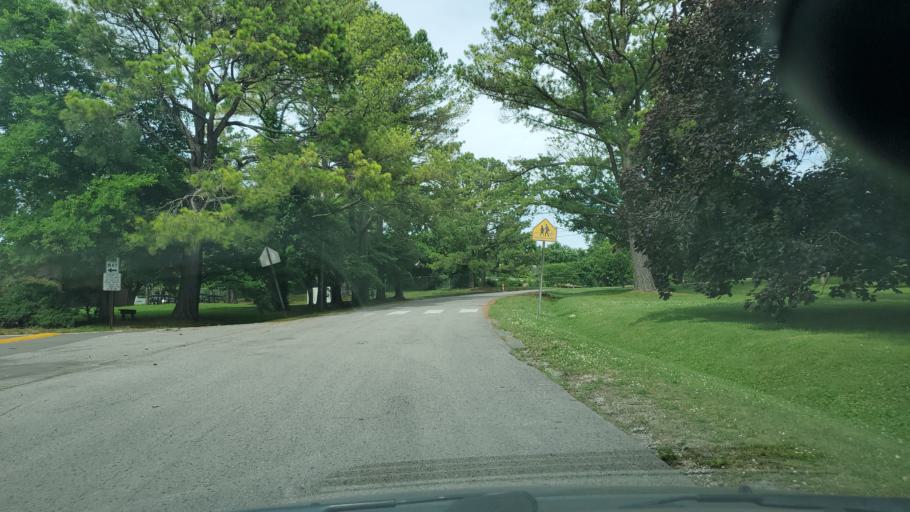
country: US
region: Tennessee
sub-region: Davidson County
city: Lakewood
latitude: 36.2026
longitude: -86.6811
